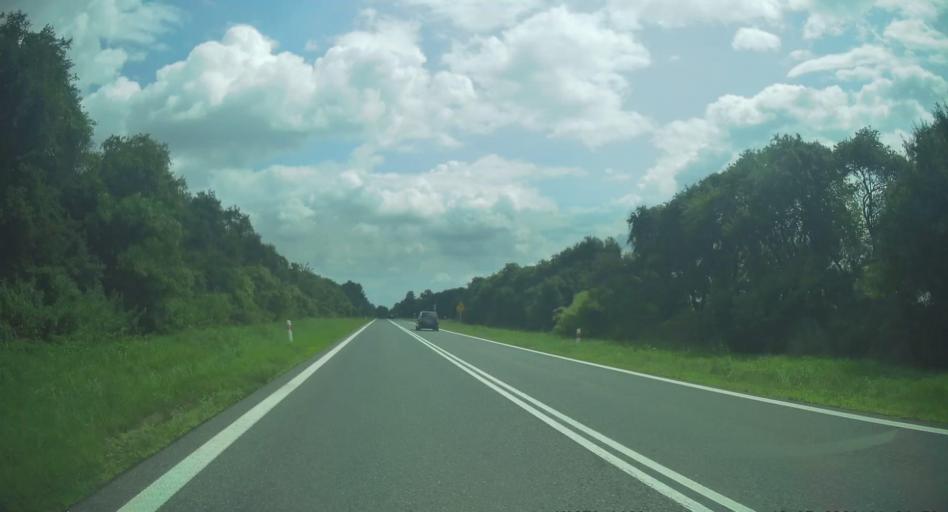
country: PL
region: Opole Voivodeship
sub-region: Powiat prudnicki
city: Lubrza
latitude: 50.3305
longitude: 17.6539
